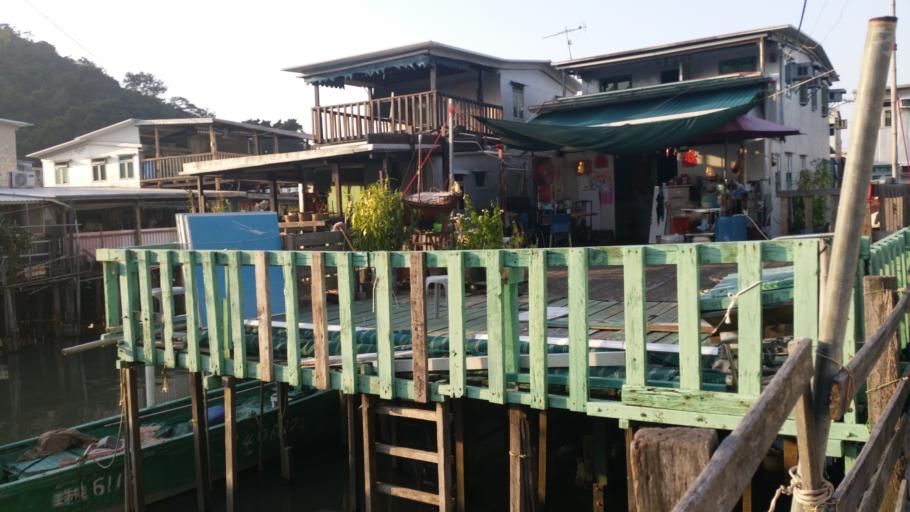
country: HK
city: Tai O
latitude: 22.2548
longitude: 113.8645
